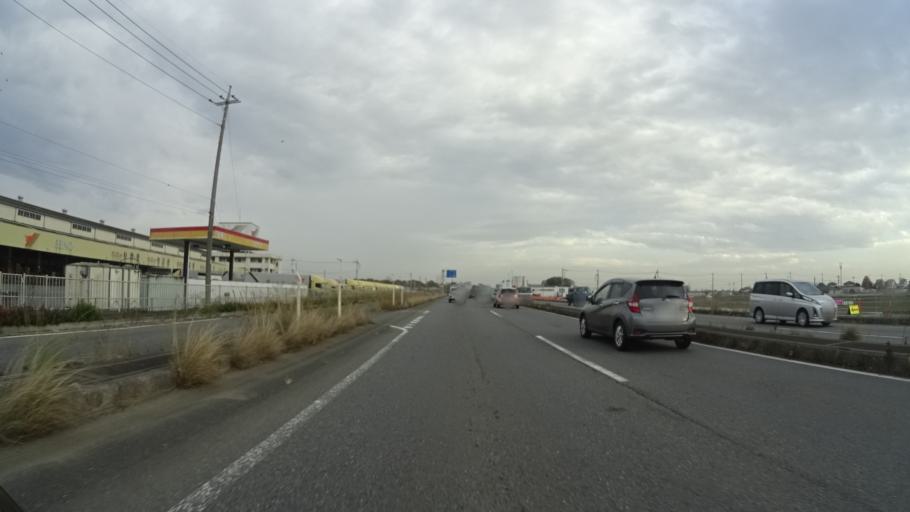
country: JP
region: Gunma
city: Isesaki
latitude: 36.3642
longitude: 139.1827
